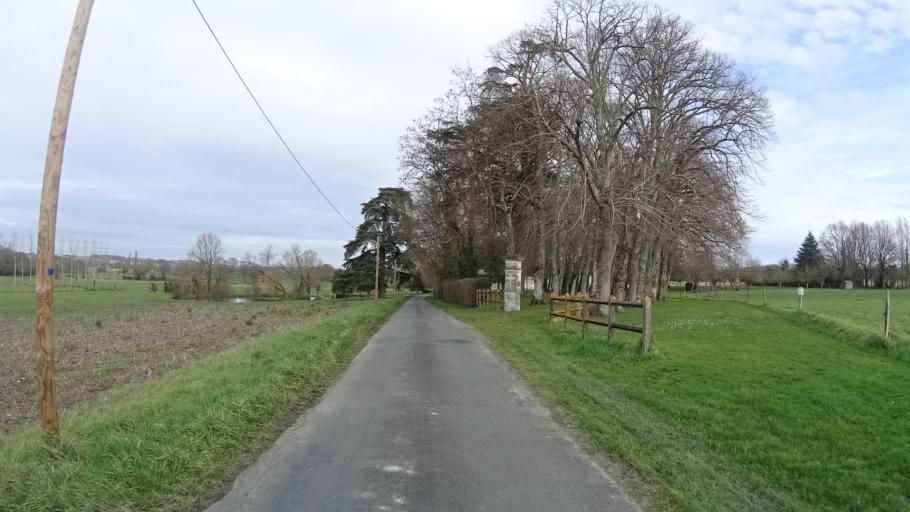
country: FR
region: Aquitaine
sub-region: Departement de la Dordogne
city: Saint-Aulaye
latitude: 45.2278
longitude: 0.1595
